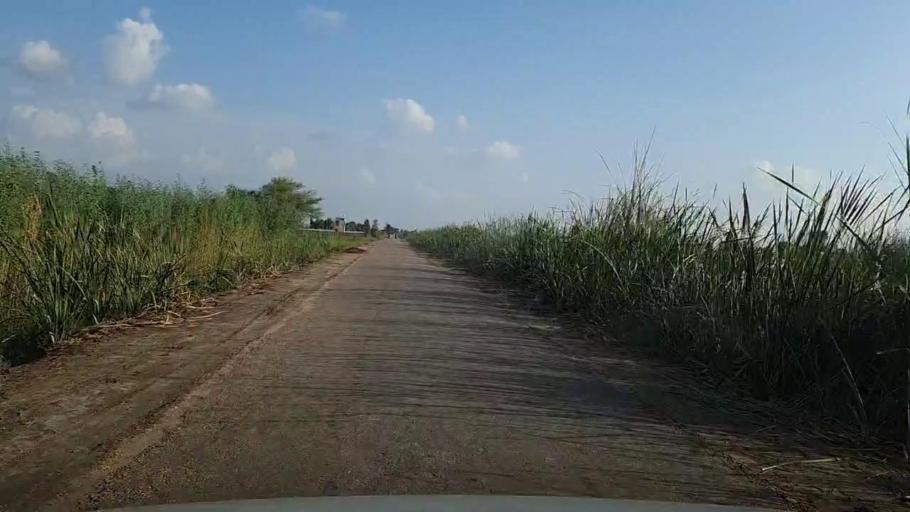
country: PK
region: Sindh
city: Hingorja
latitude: 27.0931
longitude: 68.4024
